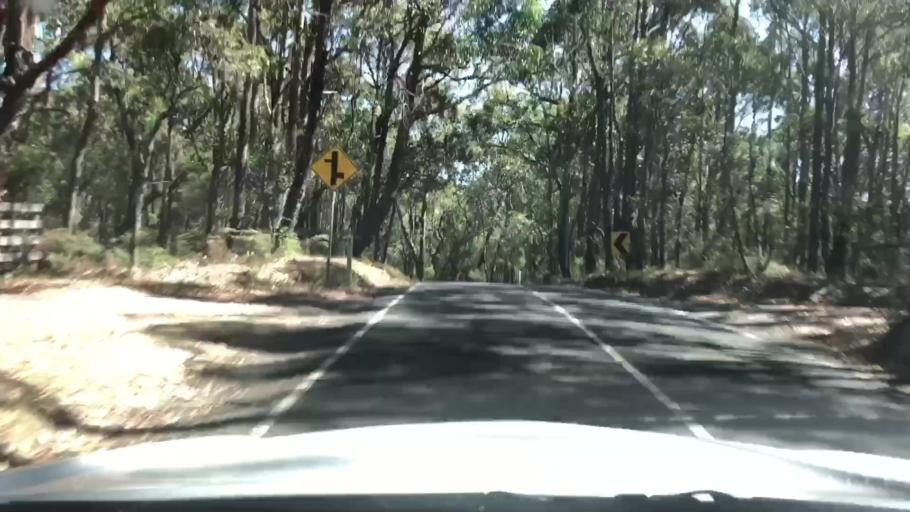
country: AU
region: Victoria
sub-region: Yarra Ranges
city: Macclesfield
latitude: -37.8601
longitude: 145.4788
